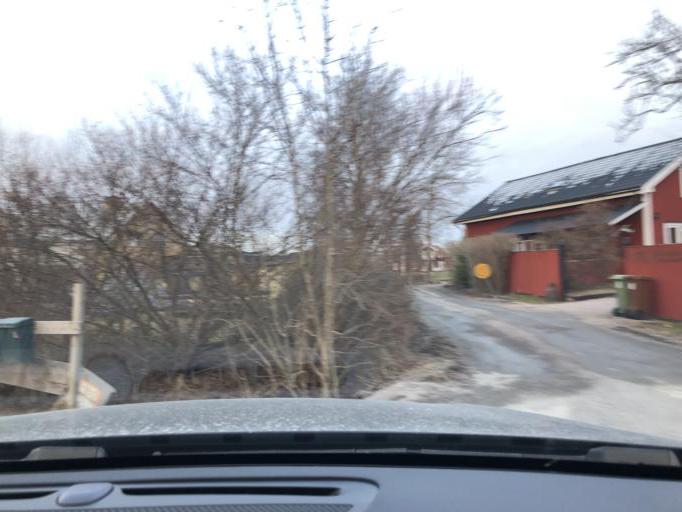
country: SE
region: Uppsala
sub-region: Uppsala Kommun
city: Gamla Uppsala
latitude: 59.9120
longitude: 17.6433
